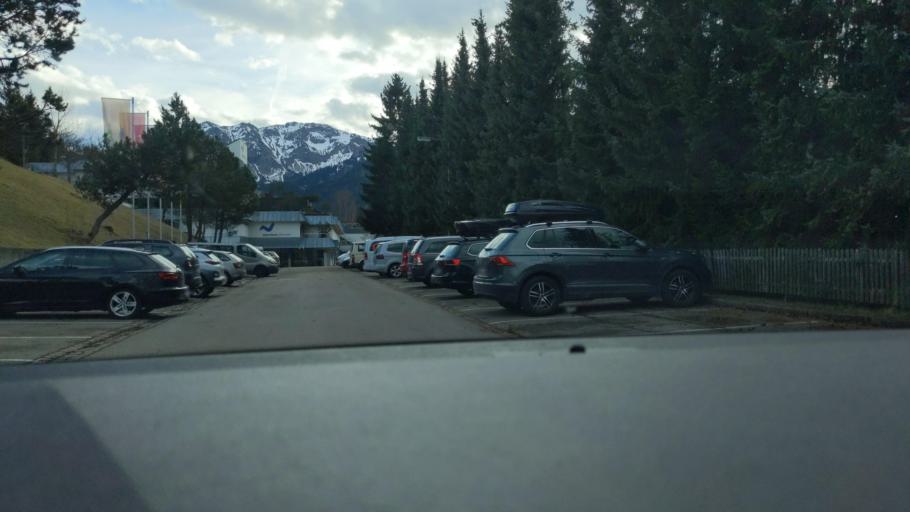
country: DE
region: Bavaria
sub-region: Swabia
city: Pfronten
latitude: 47.5820
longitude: 10.5705
